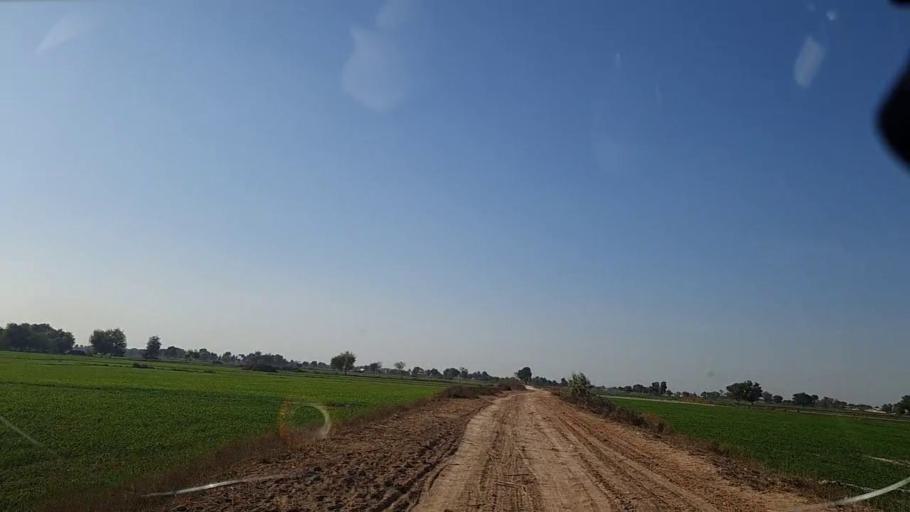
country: PK
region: Sindh
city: Khanpur
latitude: 27.7759
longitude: 69.3654
